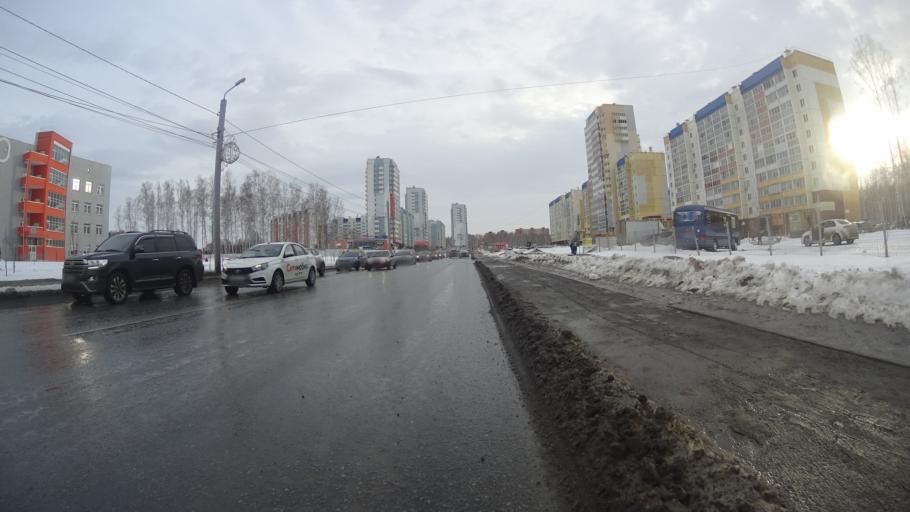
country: RU
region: Chelyabinsk
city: Roshchino
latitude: 55.2061
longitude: 61.2843
